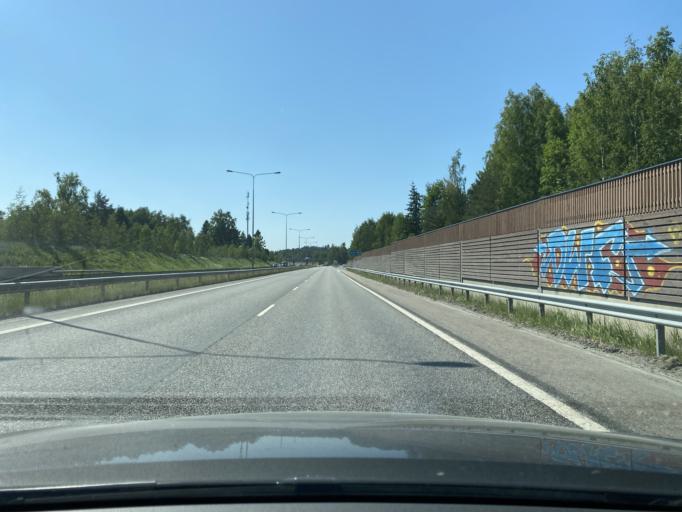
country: FI
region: Pirkanmaa
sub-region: Tampere
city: Nokia
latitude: 61.4833
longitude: 23.5634
